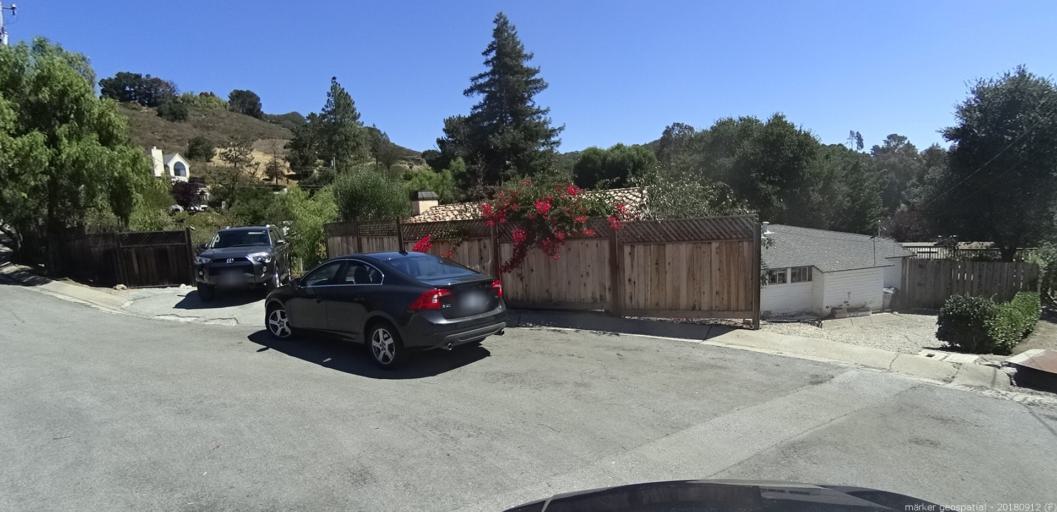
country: US
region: California
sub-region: Monterey County
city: Carmel Valley Village
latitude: 36.4930
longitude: -121.7390
